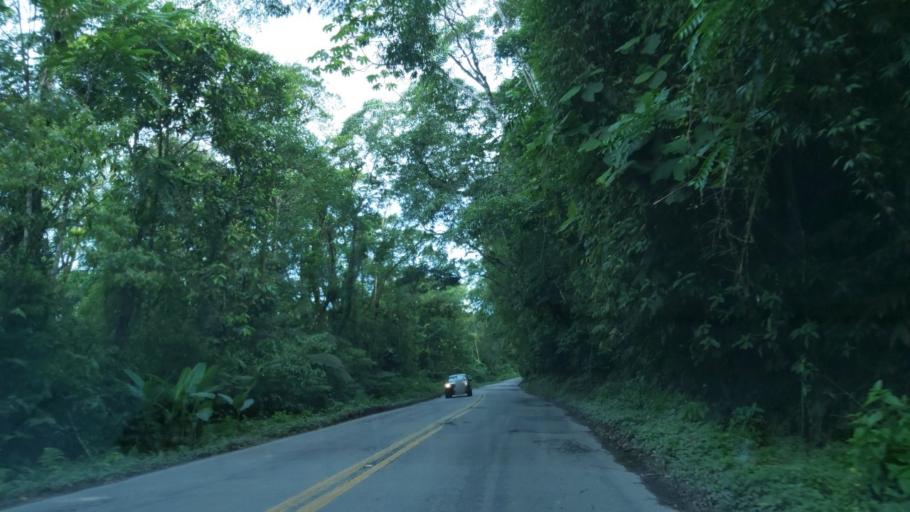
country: BR
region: Sao Paulo
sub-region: Miracatu
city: Miracatu
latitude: -24.0377
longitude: -47.5670
